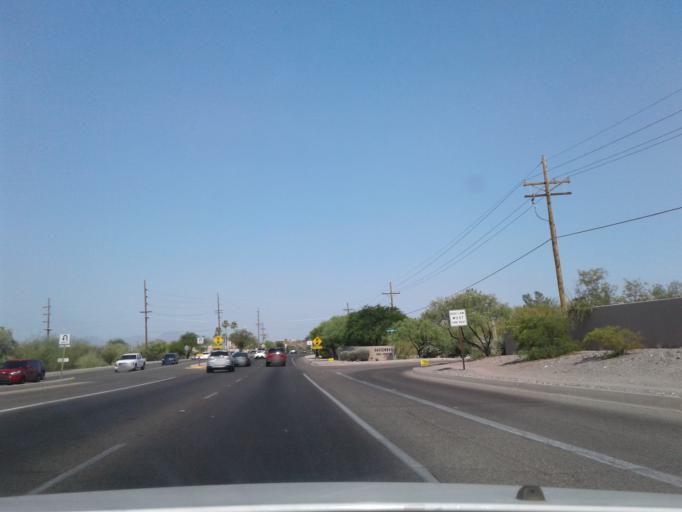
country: US
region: Arizona
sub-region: Pima County
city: Catalina Foothills
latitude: 32.3084
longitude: -110.8999
